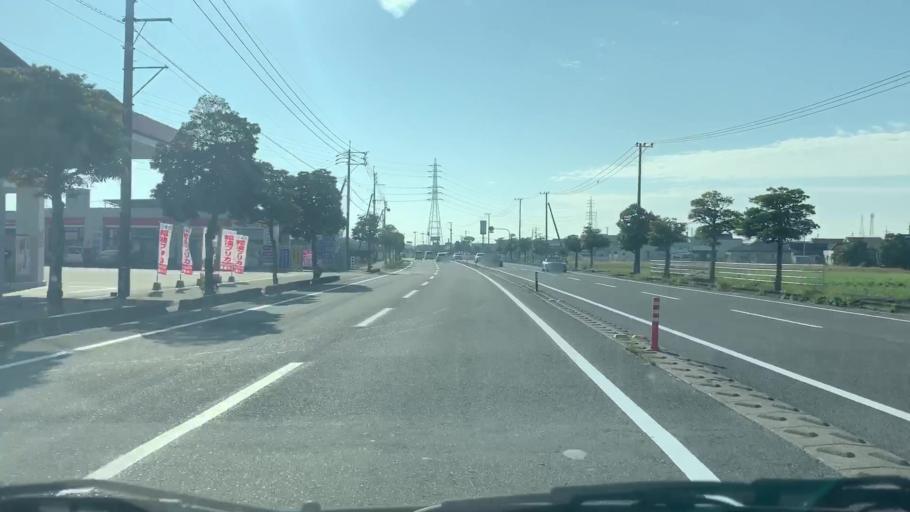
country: JP
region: Saga Prefecture
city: Saga-shi
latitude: 33.2981
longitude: 130.2813
